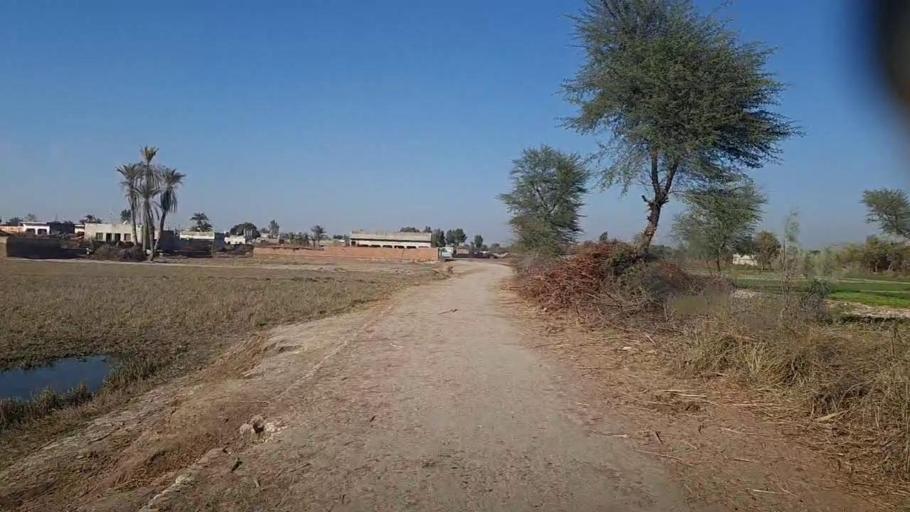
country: PK
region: Sindh
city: Khairpur
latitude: 27.9997
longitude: 69.7330
